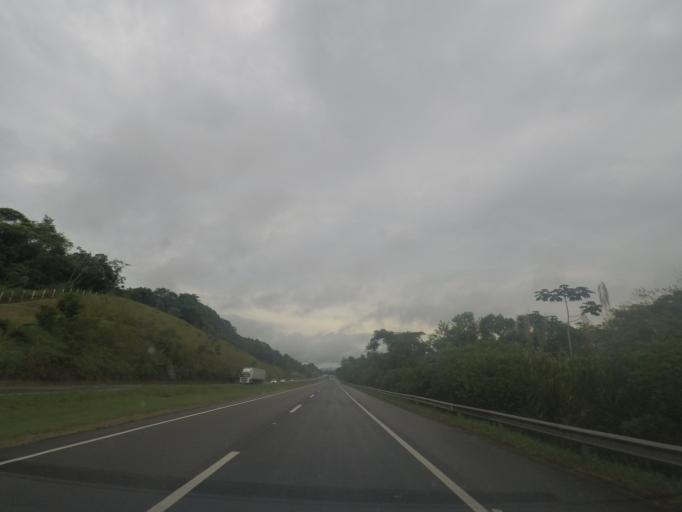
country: BR
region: Sao Paulo
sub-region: Jacupiranga
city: Jacupiranga
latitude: -24.6582
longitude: -47.9671
